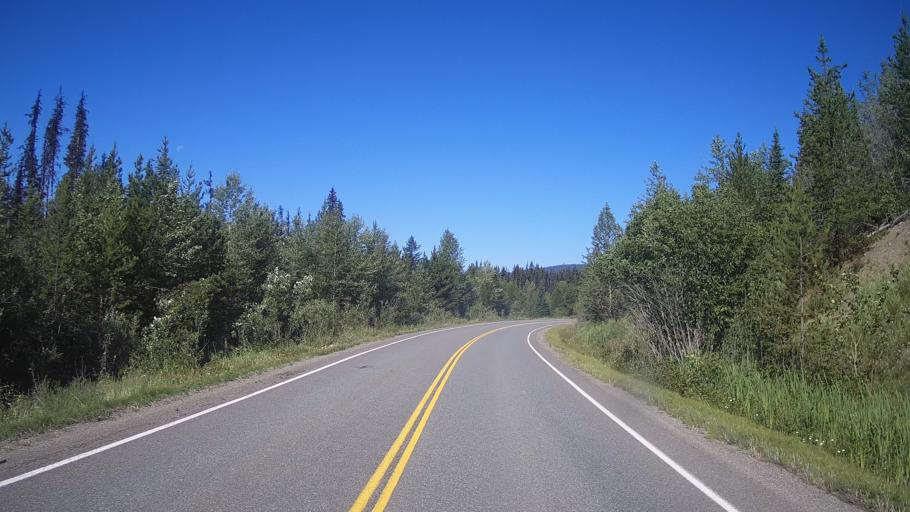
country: CA
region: British Columbia
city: Kamloops
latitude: 51.4955
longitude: -120.4141
